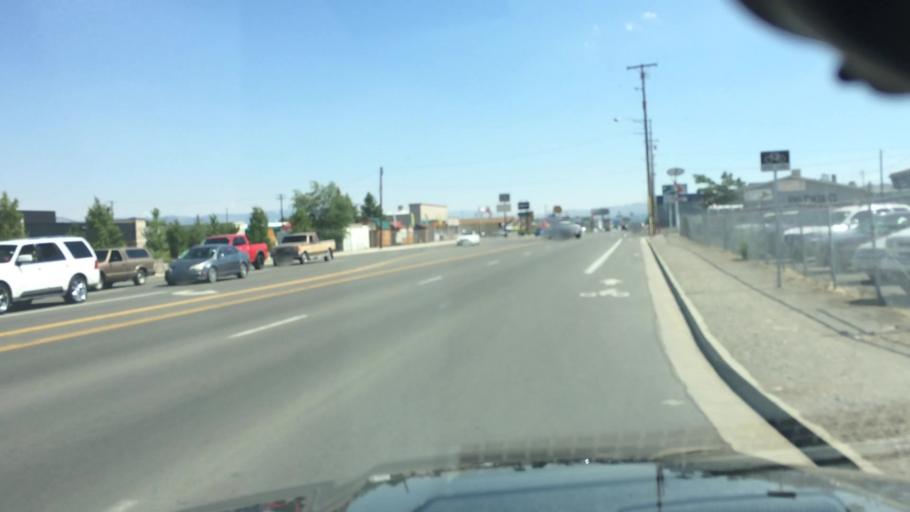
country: US
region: Nevada
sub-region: Washoe County
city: Reno
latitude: 39.5271
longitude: -119.7894
